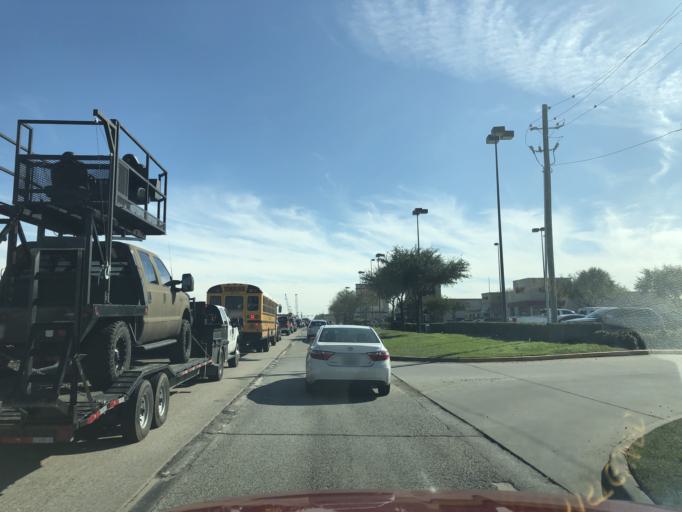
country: US
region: Texas
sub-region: Galveston County
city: League City
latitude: 29.4693
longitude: -95.0939
